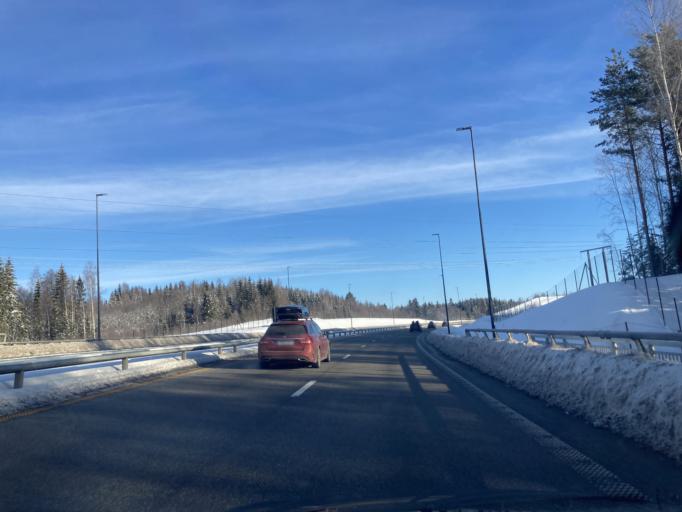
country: NO
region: Hedmark
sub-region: Loten
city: Loten
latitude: 60.8351
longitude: 11.2963
